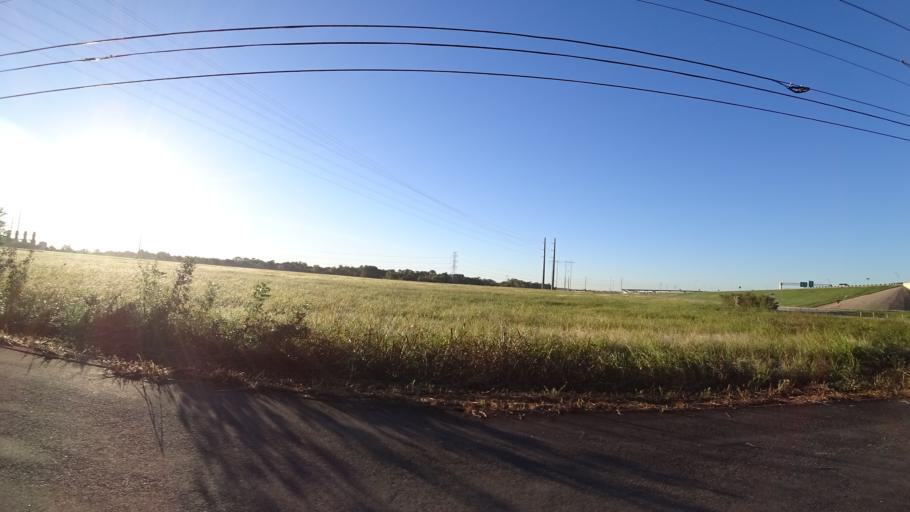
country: US
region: Texas
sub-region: Travis County
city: Hornsby Bend
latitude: 30.2097
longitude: -97.6211
